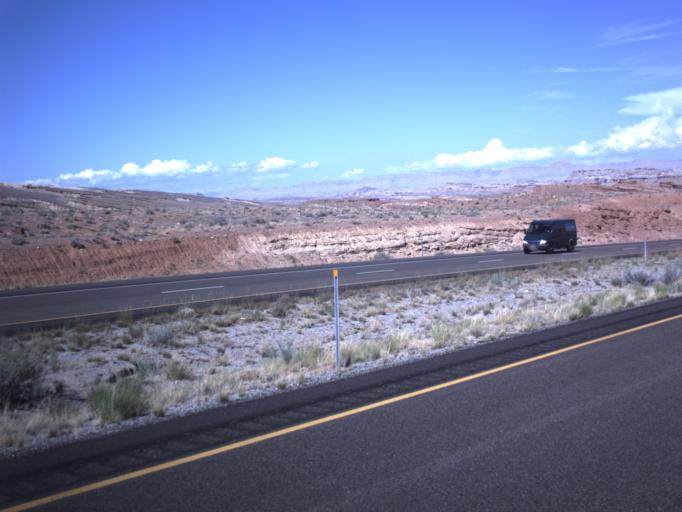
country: US
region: Utah
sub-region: Carbon County
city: East Carbon City
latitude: 38.9230
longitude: -110.4239
